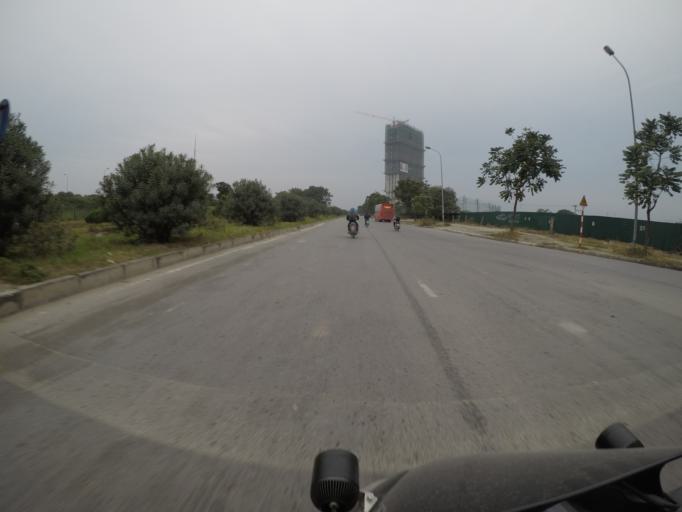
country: VN
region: Ha Noi
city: Thanh Xuan
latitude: 21.0051
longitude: 105.7730
